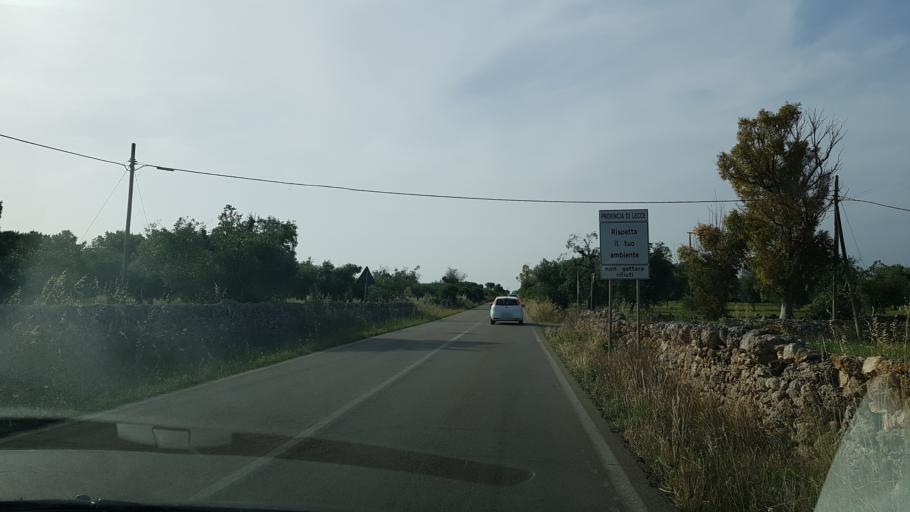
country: IT
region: Apulia
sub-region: Provincia di Lecce
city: Porto Cesareo
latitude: 40.3124
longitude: 17.8627
